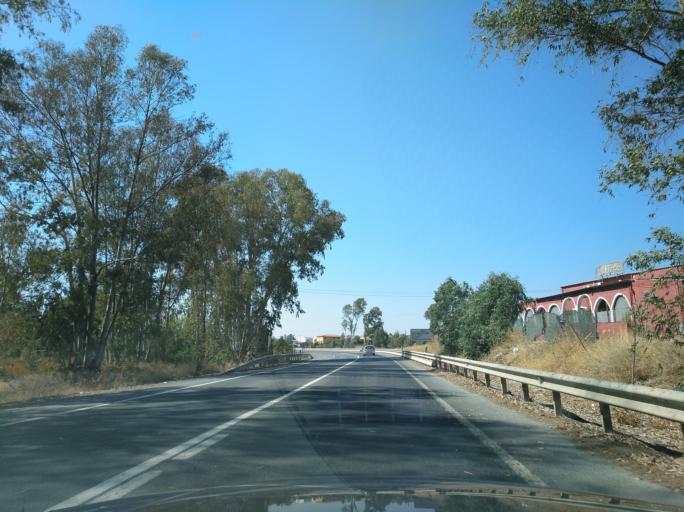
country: ES
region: Andalusia
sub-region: Provincia de Huelva
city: Gibraleon
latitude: 37.3790
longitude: -6.9841
